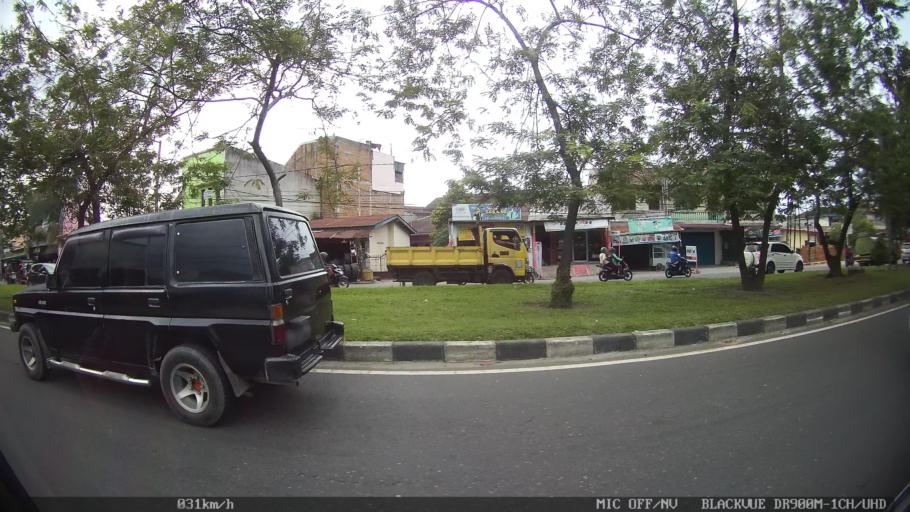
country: ID
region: North Sumatra
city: Deli Tua
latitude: 3.5409
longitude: 98.6596
